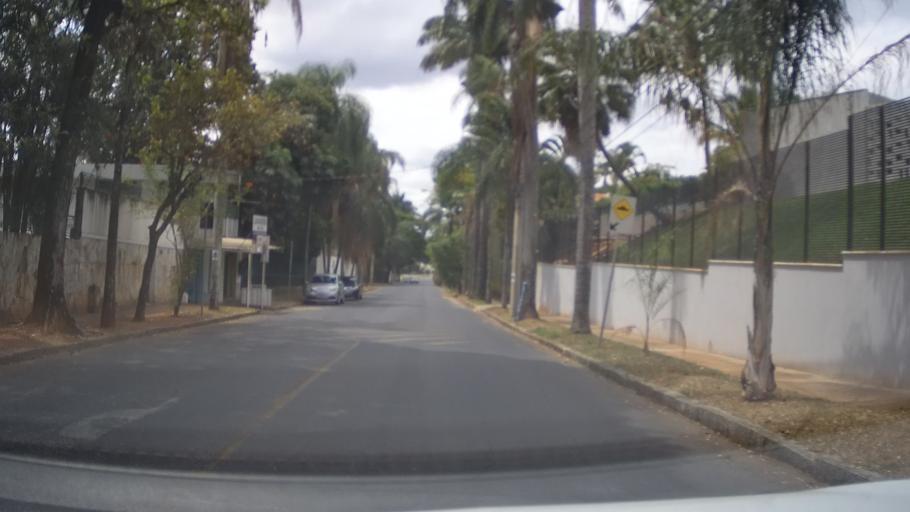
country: BR
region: Minas Gerais
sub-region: Belo Horizonte
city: Belo Horizonte
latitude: -19.8563
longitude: -43.9672
